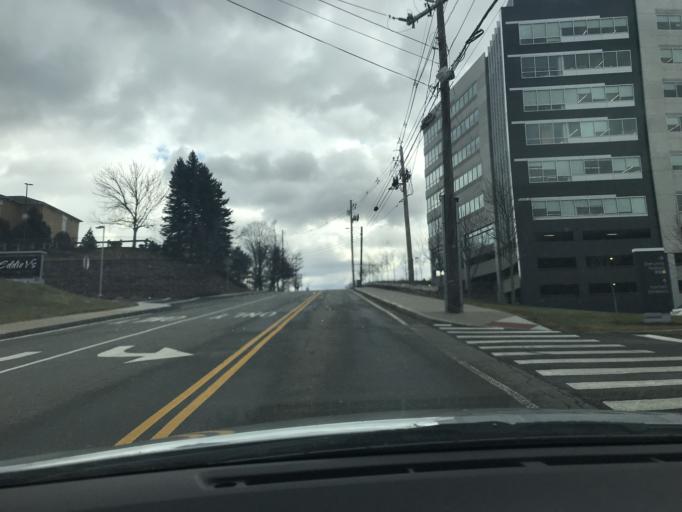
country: US
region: Massachusetts
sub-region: Middlesex County
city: Burlington
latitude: 42.4828
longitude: -71.2210
